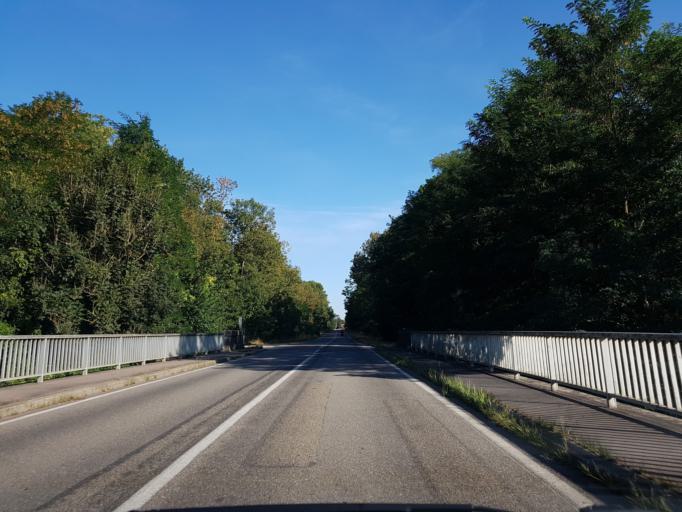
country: FR
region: Alsace
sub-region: Departement du Haut-Rhin
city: Pulversheim
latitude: 47.8430
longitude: 7.2863
